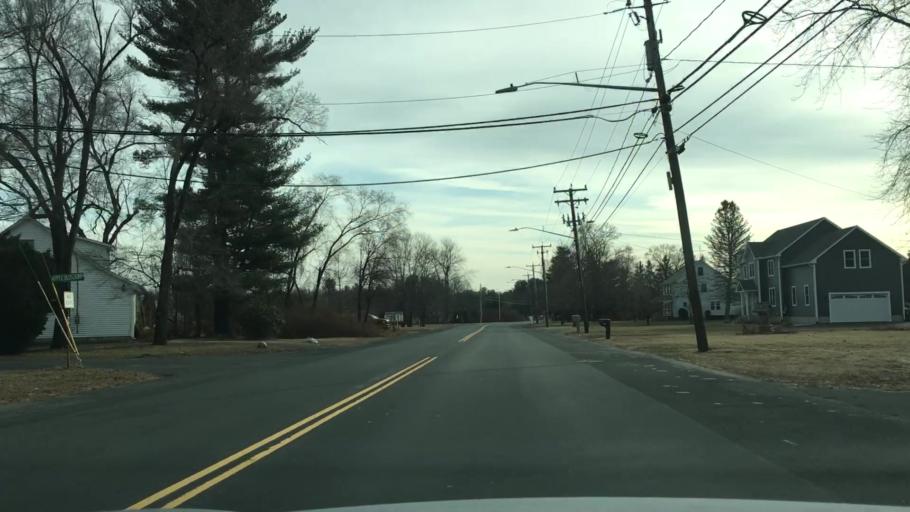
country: US
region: Massachusetts
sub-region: Hampden County
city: Westfield
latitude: 42.0931
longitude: -72.7629
